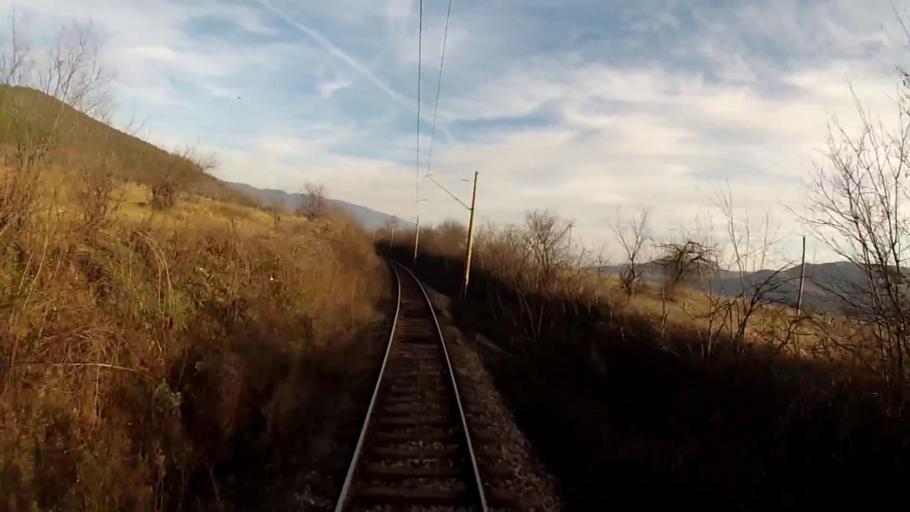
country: BG
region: Plovdiv
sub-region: Obshtina Karlovo
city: Klisura
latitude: 42.7177
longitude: 24.5819
